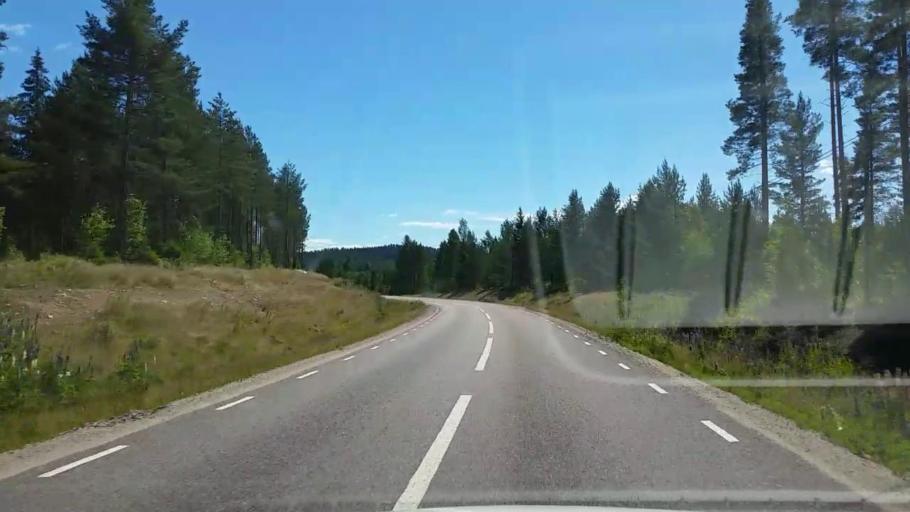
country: SE
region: Gaevleborg
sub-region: Ovanakers Kommun
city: Edsbyn
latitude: 61.4295
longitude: 15.7202
